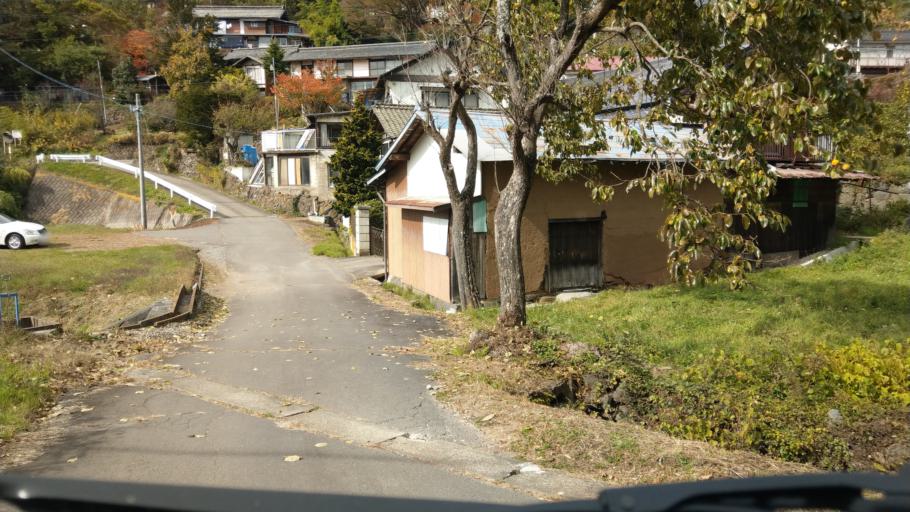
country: JP
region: Nagano
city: Komoro
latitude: 36.3524
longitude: 138.4339
